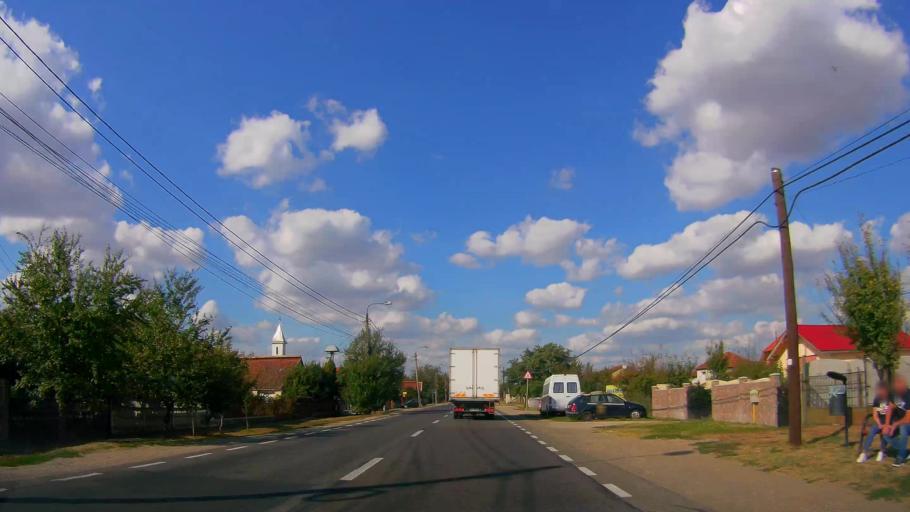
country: RO
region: Satu Mare
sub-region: Oras Ardud
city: Madaras
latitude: 47.7368
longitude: 22.8826
